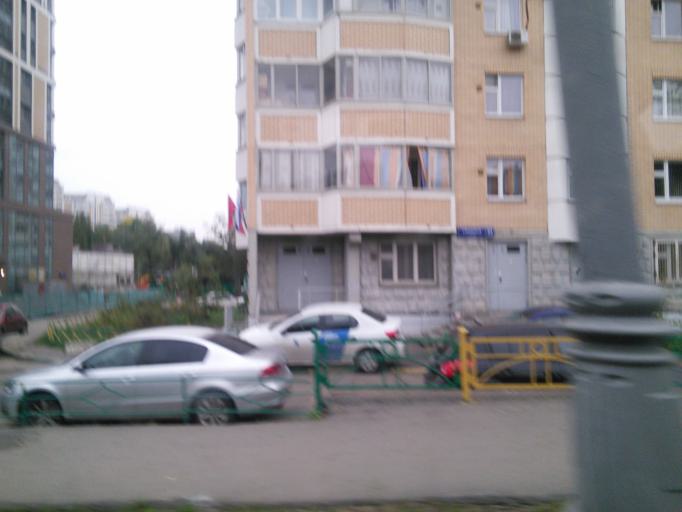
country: RU
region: Moskovskaya
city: Levoberezhnyy
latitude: 55.8644
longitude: 37.4780
